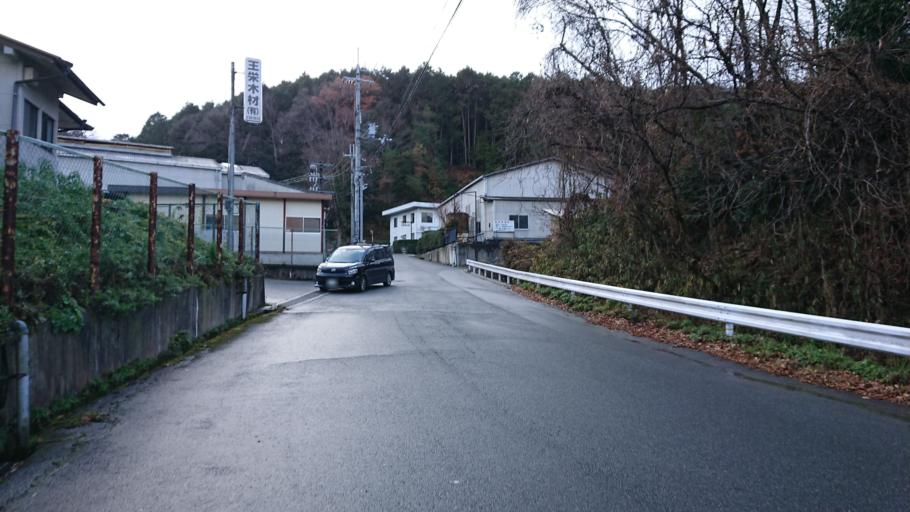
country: JP
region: Kyoto
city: Kameoka
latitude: 35.0512
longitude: 135.5185
